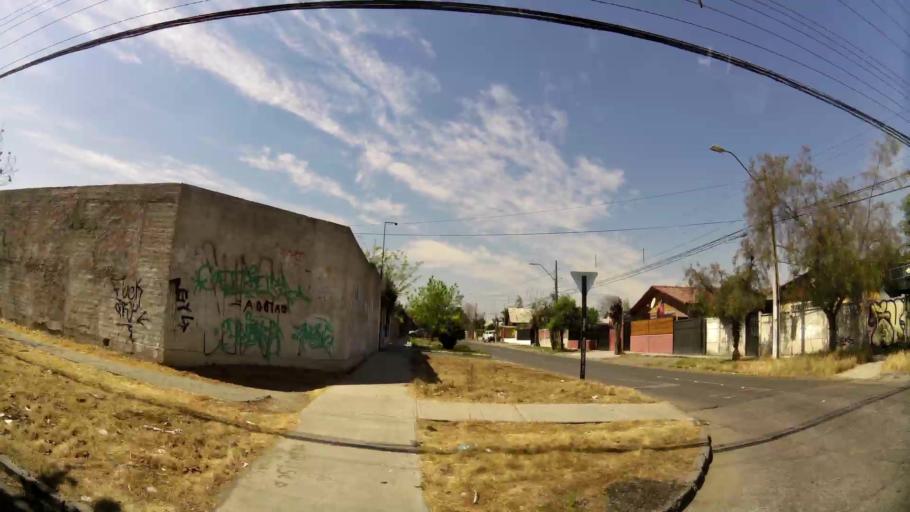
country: CL
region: Santiago Metropolitan
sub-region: Provincia de Santiago
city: La Pintana
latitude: -33.5443
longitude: -70.6633
